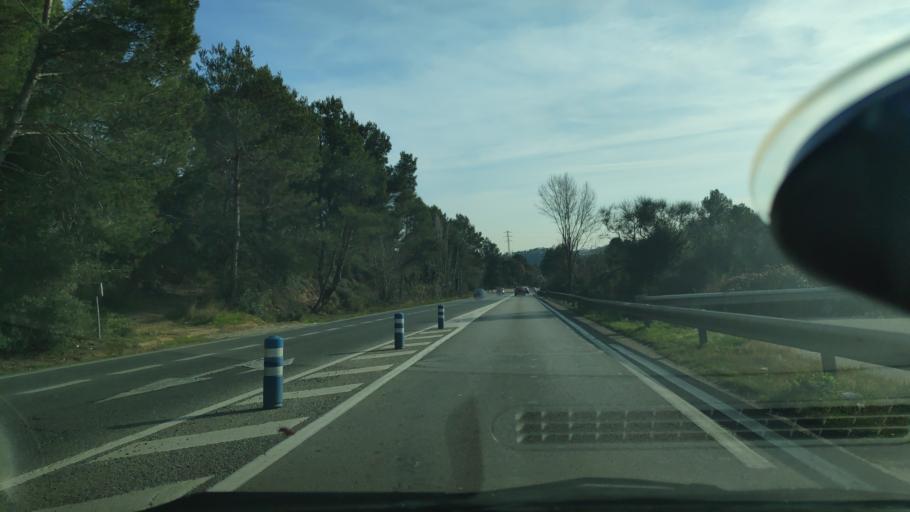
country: ES
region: Catalonia
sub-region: Provincia de Barcelona
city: Castellar del Valles
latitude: 41.5790
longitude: 2.0921
